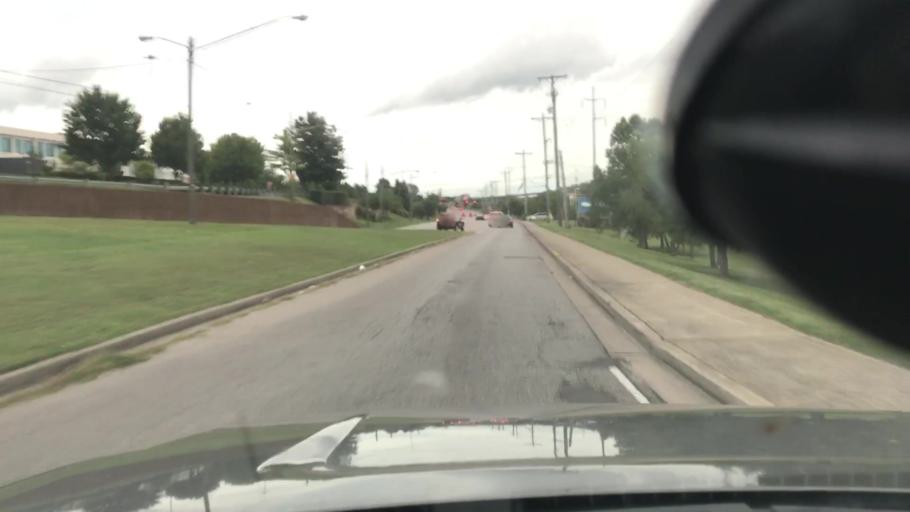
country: US
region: Tennessee
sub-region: Davidson County
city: Oak Hill
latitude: 36.1117
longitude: -86.7677
